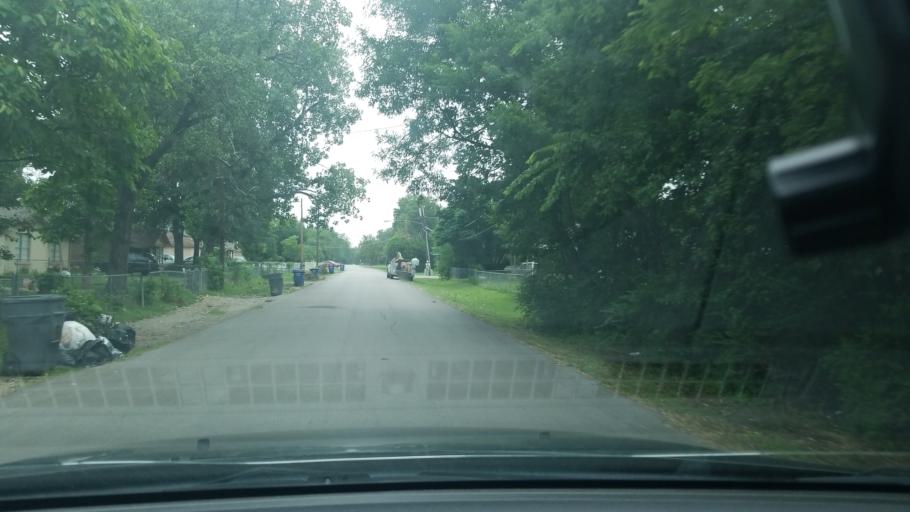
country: US
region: Texas
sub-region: Dallas County
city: Balch Springs
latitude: 32.7561
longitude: -96.6772
